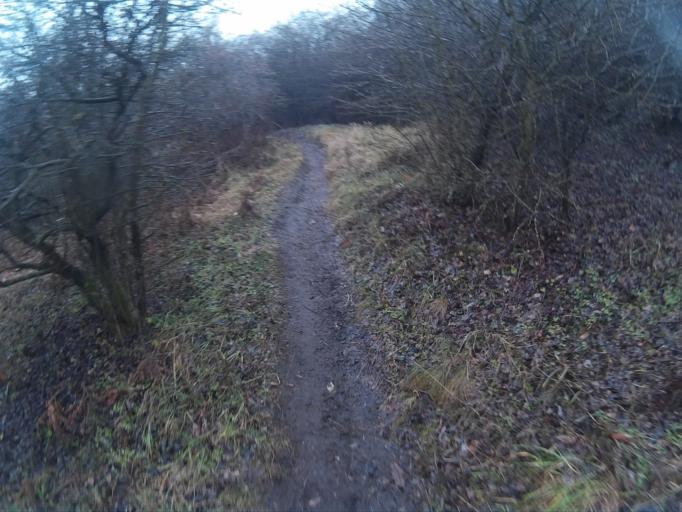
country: HU
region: Komarom-Esztergom
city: Tokod
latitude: 47.7137
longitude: 18.6494
